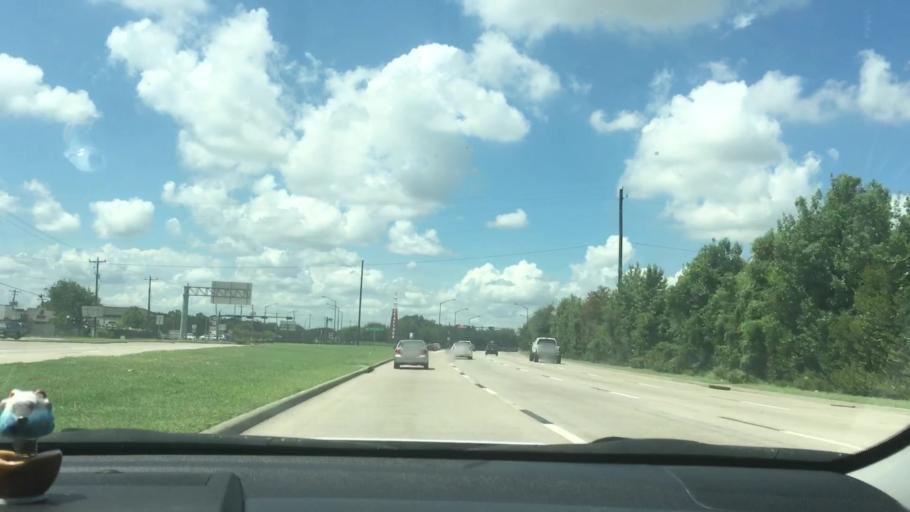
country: US
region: Texas
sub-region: Fort Bend County
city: Missouri City
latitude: 29.6164
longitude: -95.5451
